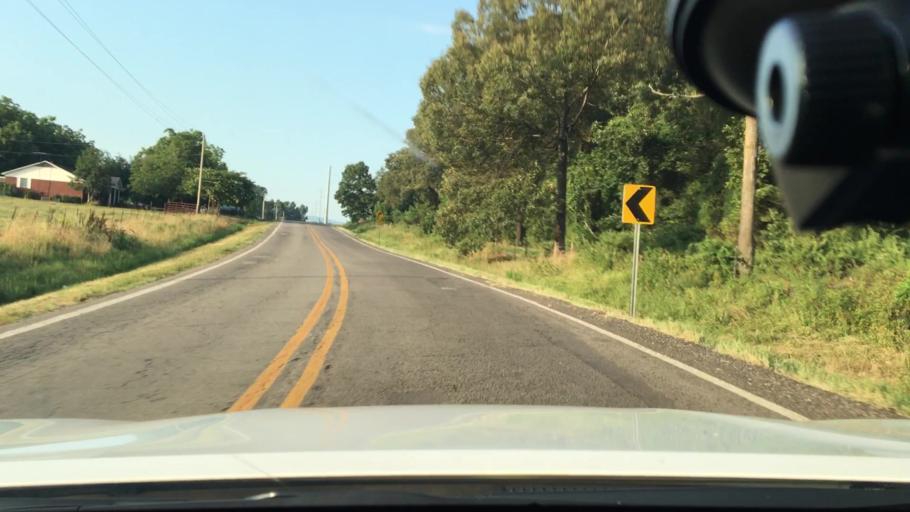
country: US
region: Arkansas
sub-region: Johnson County
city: Coal Hill
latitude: 35.3781
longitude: -93.5613
